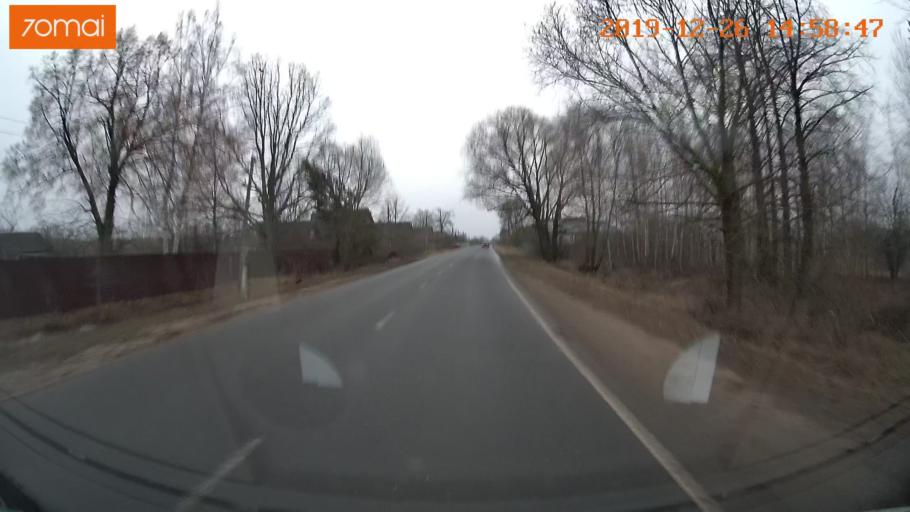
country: RU
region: Jaroslavl
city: Rybinsk
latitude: 58.2656
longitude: 38.8527
